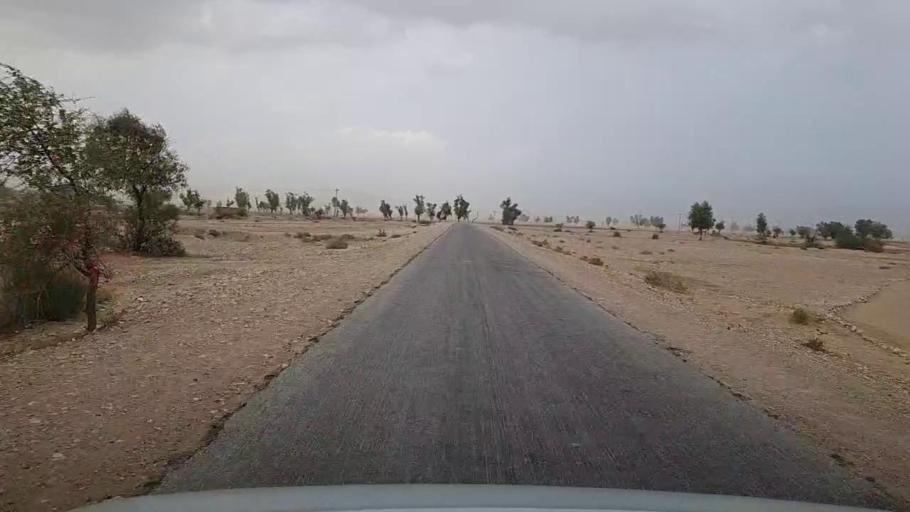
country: PK
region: Sindh
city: Sehwan
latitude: 26.3196
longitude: 67.7293
